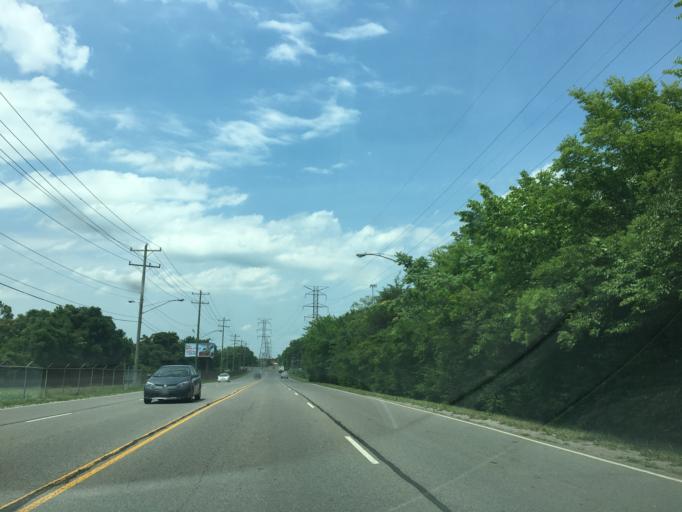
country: US
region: Tennessee
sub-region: Davidson County
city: Nashville
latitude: 36.1306
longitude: -86.7599
